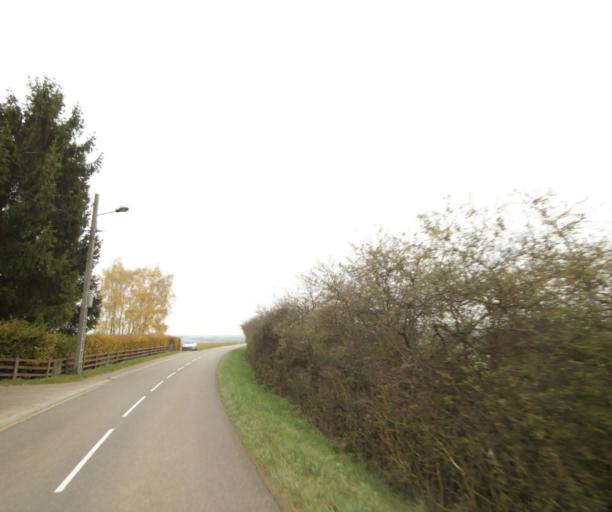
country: FR
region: Lorraine
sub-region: Departement de Meurthe-et-Moselle
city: Mancieulles
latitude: 49.2785
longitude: 5.8800
